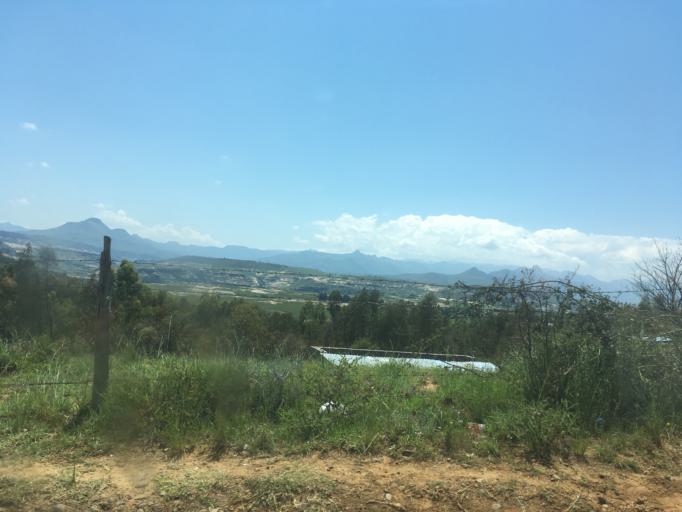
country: LS
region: Butha-Buthe
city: Butha-Buthe
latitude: -28.7231
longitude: 28.3594
